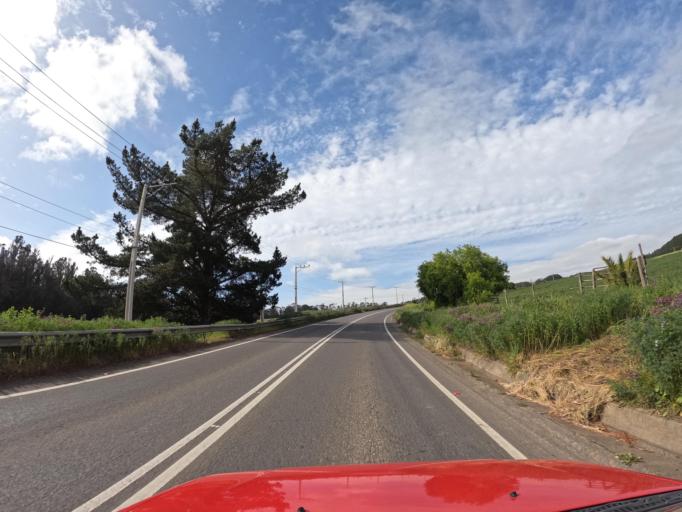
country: CL
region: O'Higgins
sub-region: Provincia de Colchagua
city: Santa Cruz
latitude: -34.3682
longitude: -71.9651
